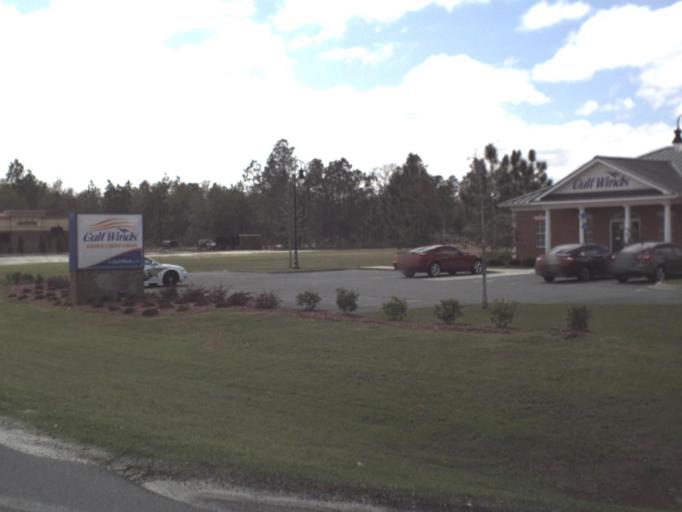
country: US
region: Florida
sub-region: Wakulla County
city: Crawfordville
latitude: 30.2103
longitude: -84.3650
